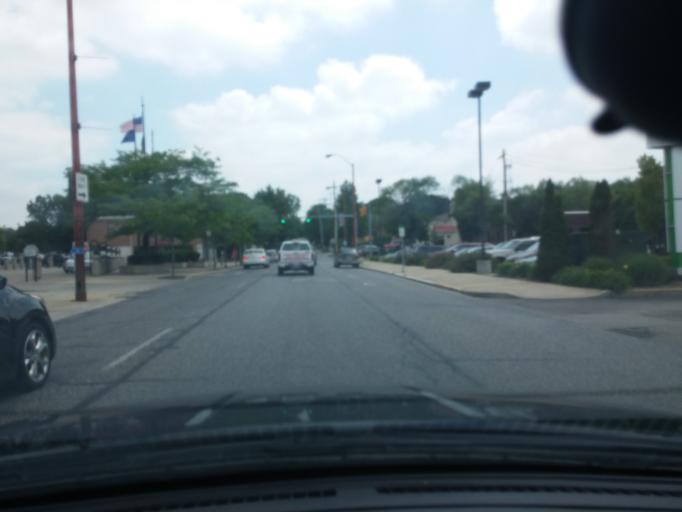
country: US
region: Indiana
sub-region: Tippecanoe County
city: Lafayette
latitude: 40.4173
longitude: -86.8915
